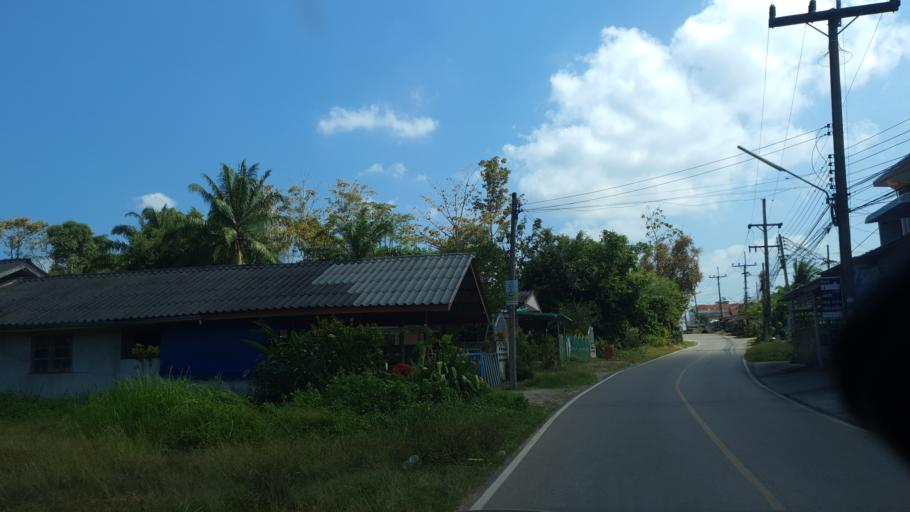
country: TH
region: Krabi
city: Nuea Khlong
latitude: 8.0839
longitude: 98.9879
